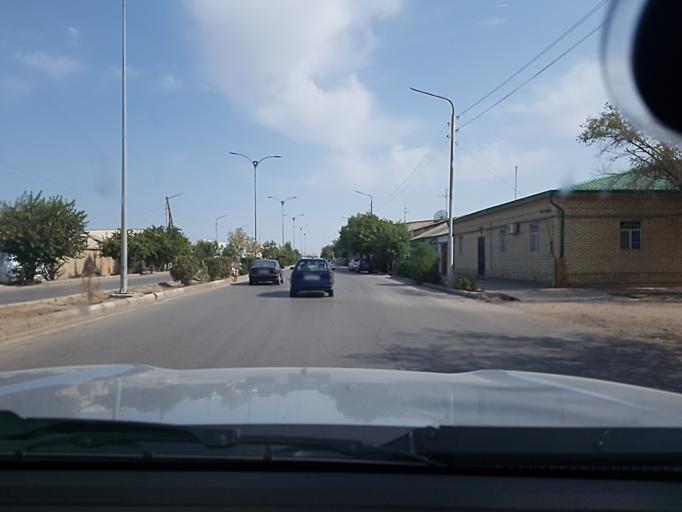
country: TM
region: Dasoguz
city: Dasoguz
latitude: 41.8333
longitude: 59.9824
